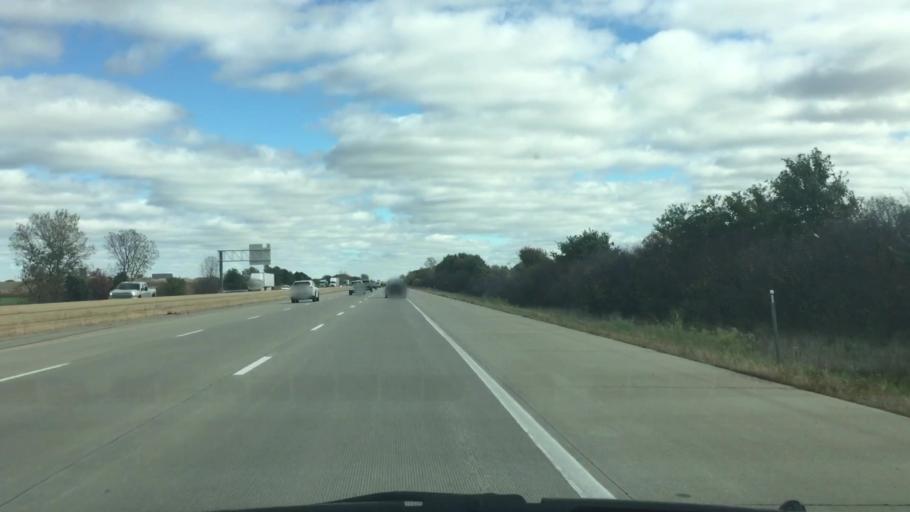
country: US
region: Iowa
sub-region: Johnson County
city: Iowa City
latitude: 41.6831
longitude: -91.4771
